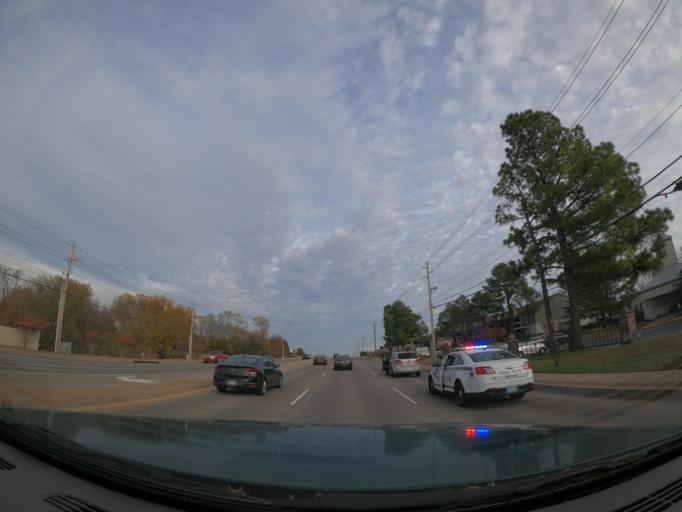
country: US
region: Oklahoma
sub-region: Tulsa County
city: Jenks
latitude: 36.0608
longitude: -95.9111
